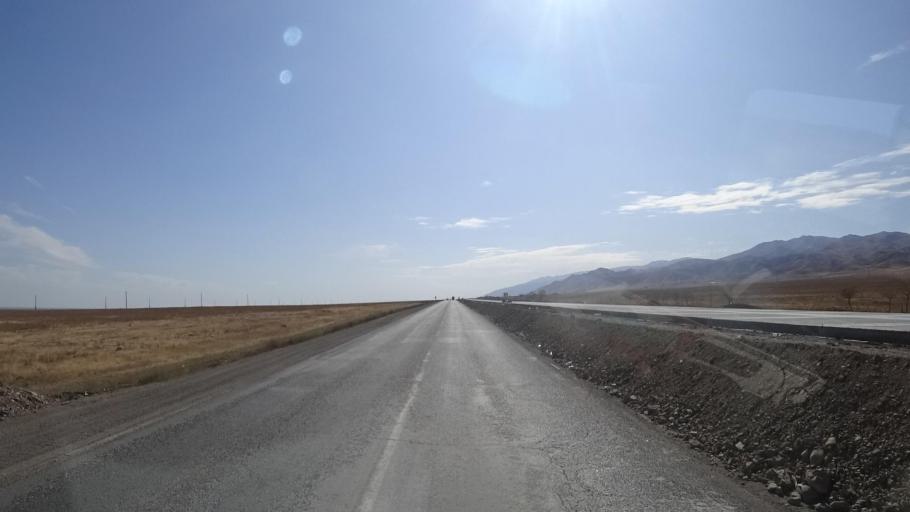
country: KG
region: Chuy
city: Ivanovka
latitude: 43.3988
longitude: 75.1187
